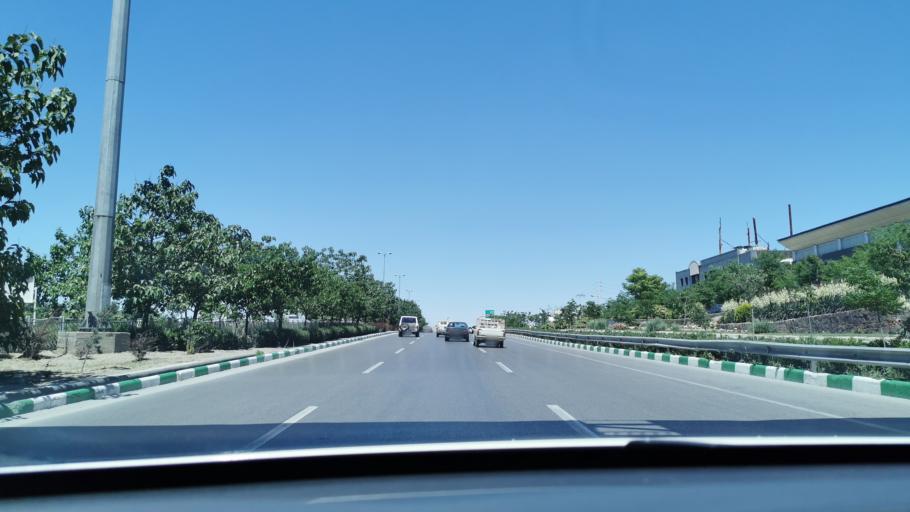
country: IR
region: Razavi Khorasan
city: Mashhad
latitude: 36.2637
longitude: 59.6520
